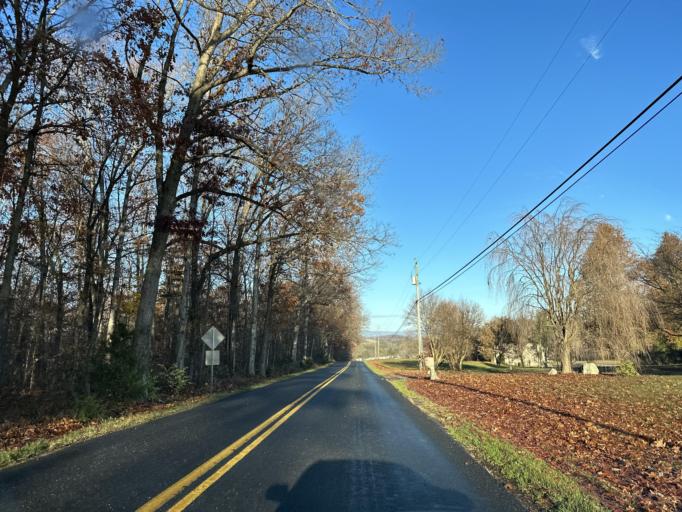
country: US
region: Virginia
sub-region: Augusta County
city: Weyers Cave
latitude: 38.2968
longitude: -78.9504
